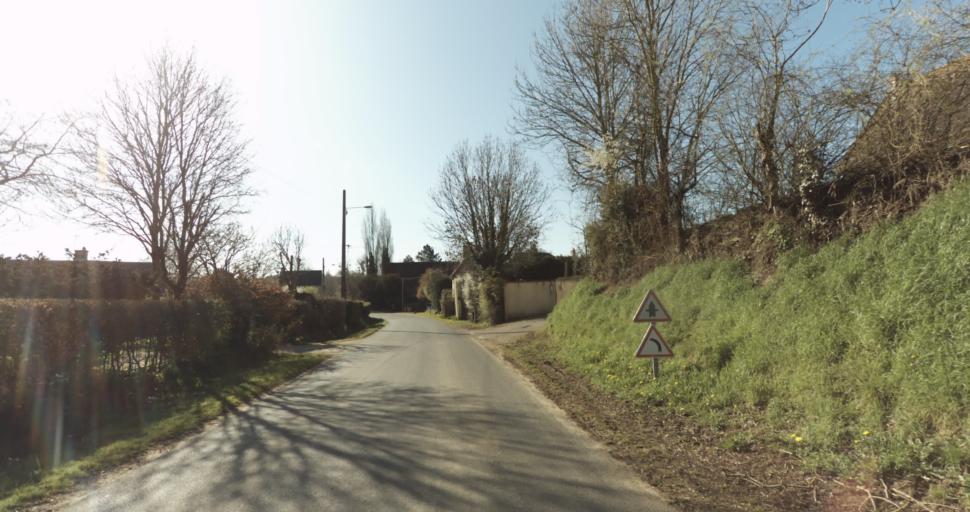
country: FR
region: Lower Normandy
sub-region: Departement du Calvados
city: Saint-Pierre-sur-Dives
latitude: 48.9760
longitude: 0.0367
